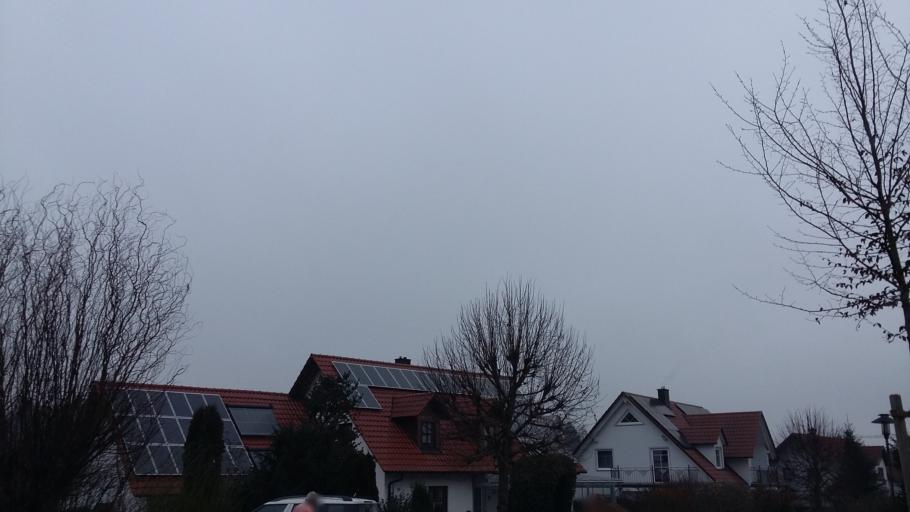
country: DE
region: Bavaria
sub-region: Swabia
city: Pottmes
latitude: 48.5842
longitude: 11.0816
